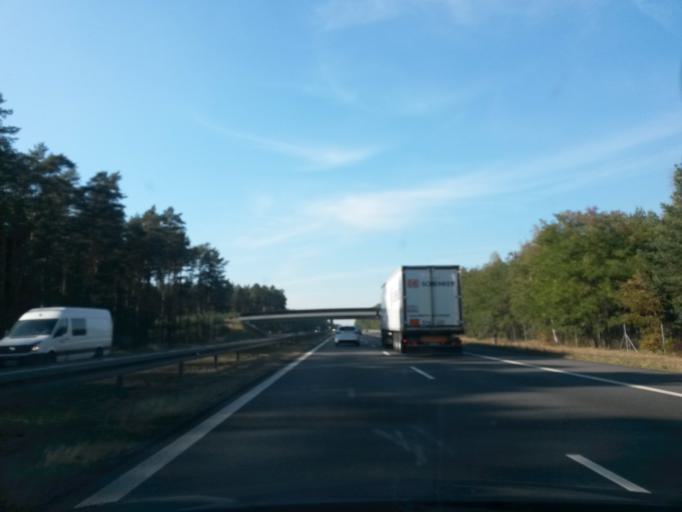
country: PL
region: Opole Voivodeship
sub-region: Powiat opolski
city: Dabrowa
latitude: 50.6223
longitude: 17.7591
